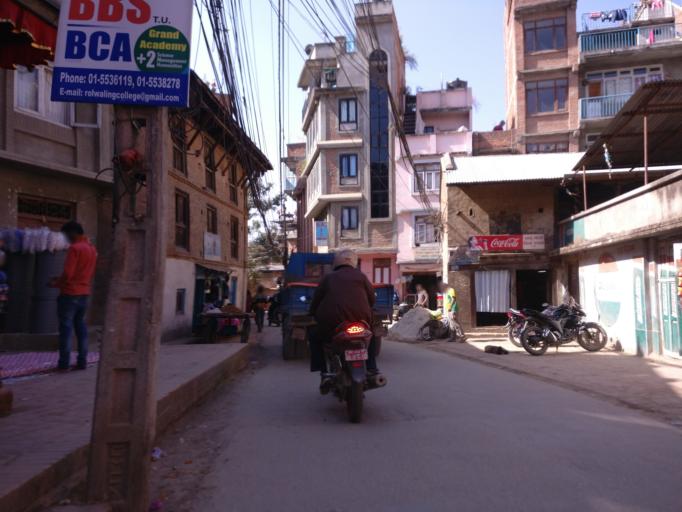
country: NP
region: Central Region
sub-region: Bagmati Zone
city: Patan
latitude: 27.6766
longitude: 85.3272
